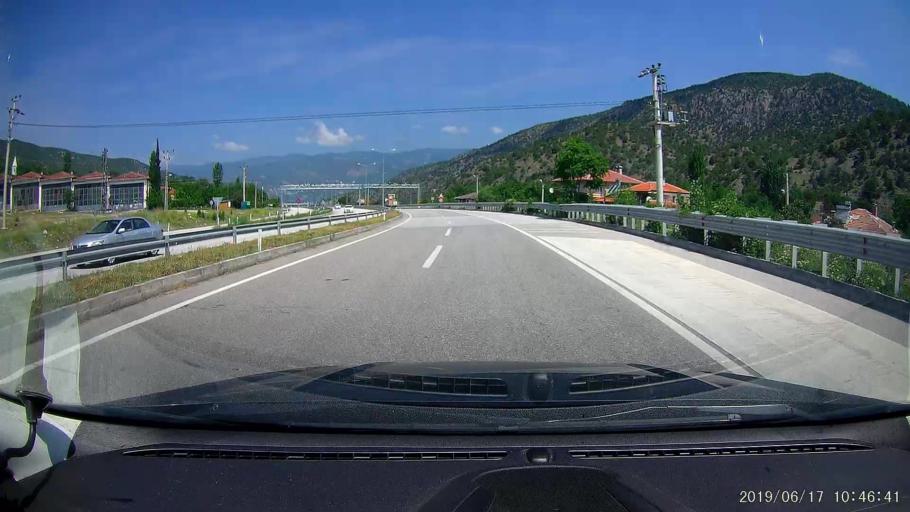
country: TR
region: Corum
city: Hacihamza
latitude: 41.0704
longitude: 34.4588
